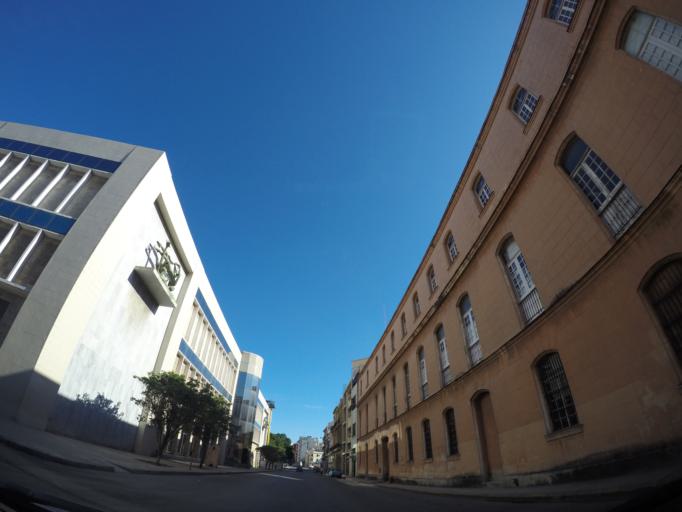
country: CU
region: La Habana
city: Centro Habana
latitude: 23.1394
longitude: -82.3571
